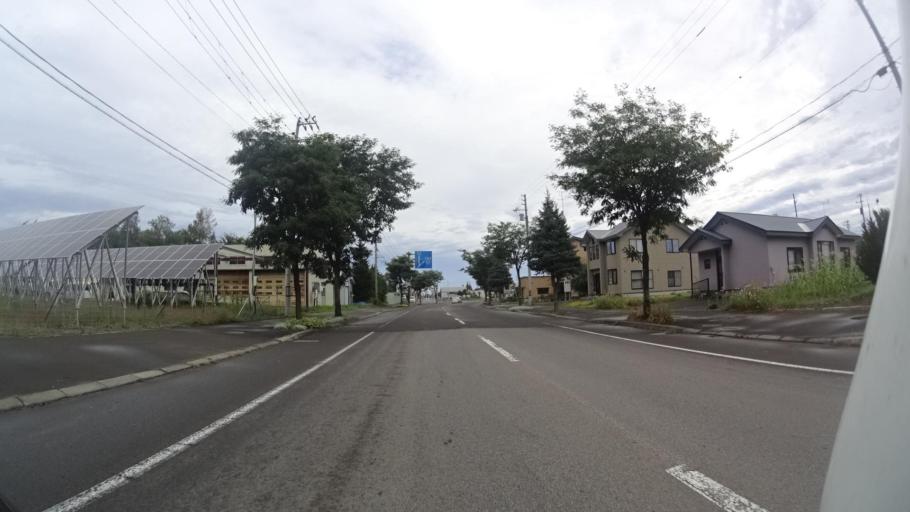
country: JP
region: Hokkaido
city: Abashiri
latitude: 43.8403
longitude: 144.5959
